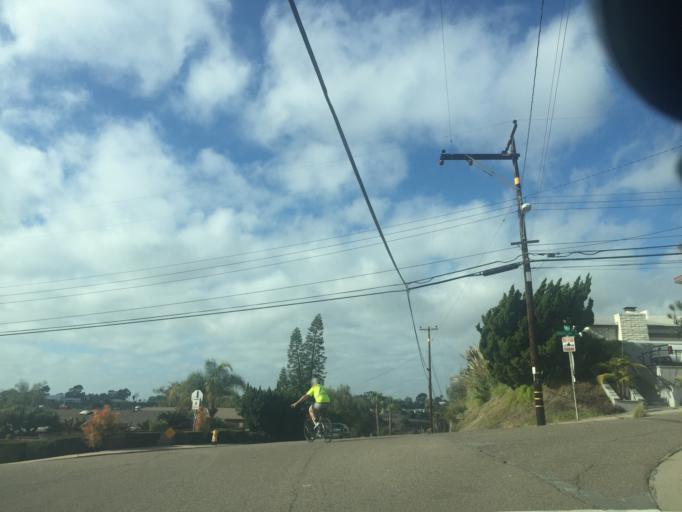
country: US
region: California
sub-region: San Diego County
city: San Diego
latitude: 32.7845
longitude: -117.1498
